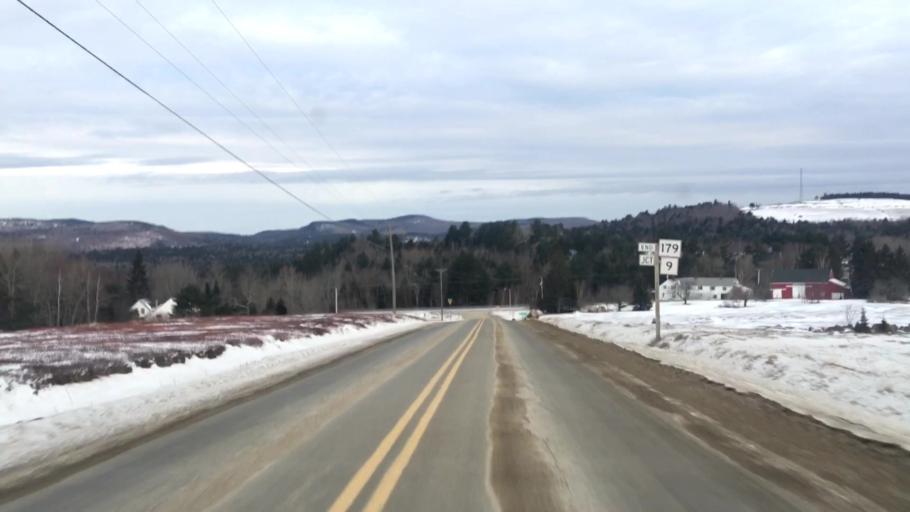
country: US
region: Maine
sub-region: Hancock County
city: Franklin
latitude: 44.8476
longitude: -68.3292
